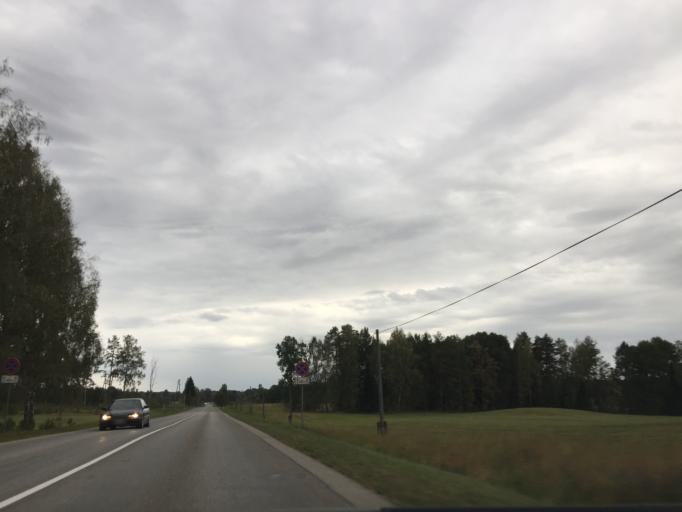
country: LV
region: Krimulda
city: Ragana
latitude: 57.1959
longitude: 24.7058
